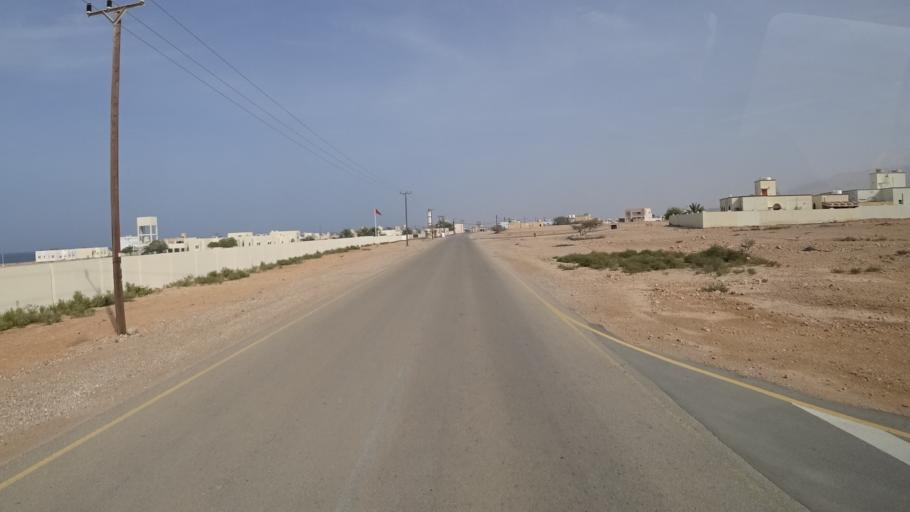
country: OM
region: Ash Sharqiyah
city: Sur
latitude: 22.9930
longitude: 59.1334
